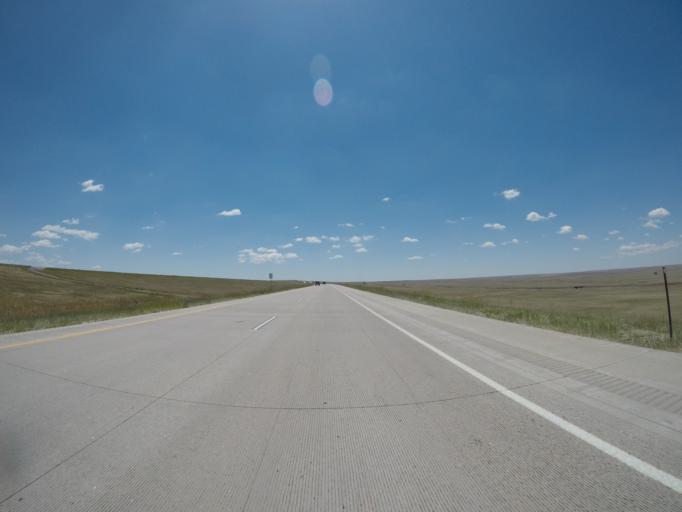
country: US
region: Colorado
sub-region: Lincoln County
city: Limon
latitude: 39.3816
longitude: -103.8891
